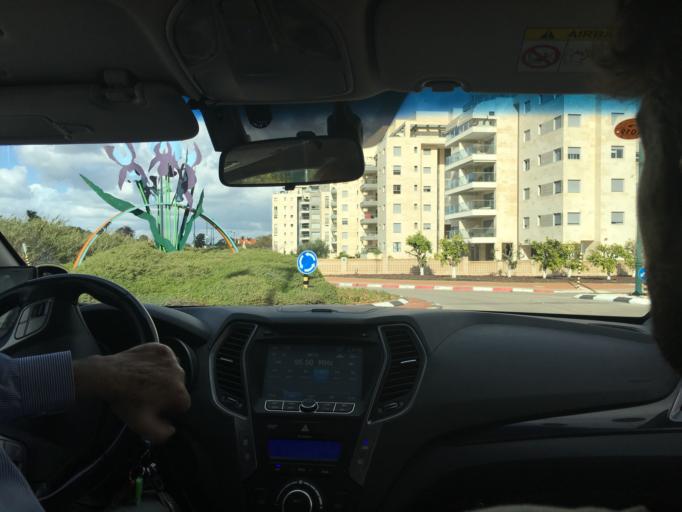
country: IL
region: Central District
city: Ness Ziona
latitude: 31.9307
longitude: 34.7853
